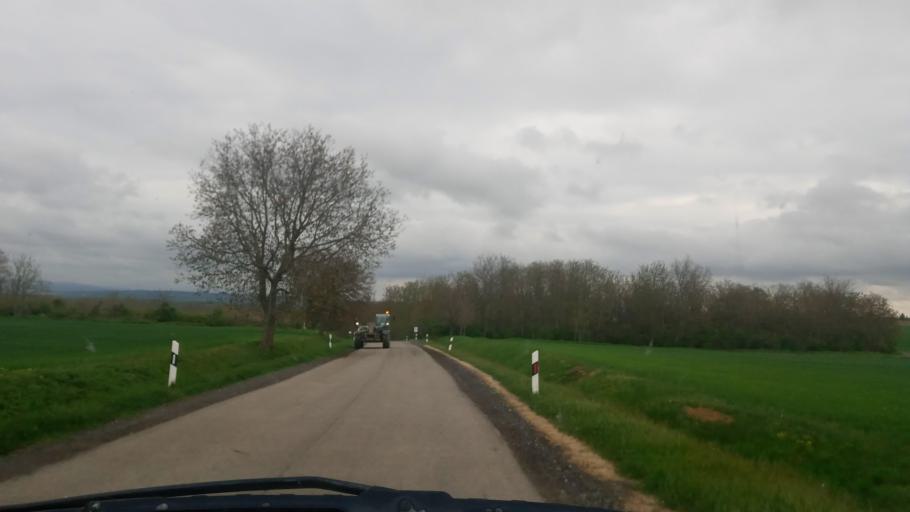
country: HU
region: Baranya
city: Kozarmisleny
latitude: 46.0343
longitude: 18.3470
